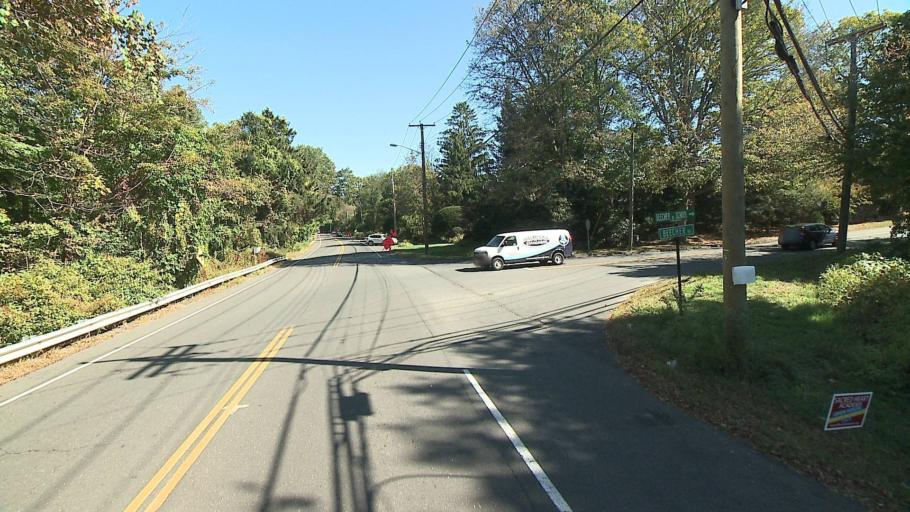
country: US
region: Connecticut
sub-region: New Haven County
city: Woodbridge
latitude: 41.3529
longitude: -73.0087
